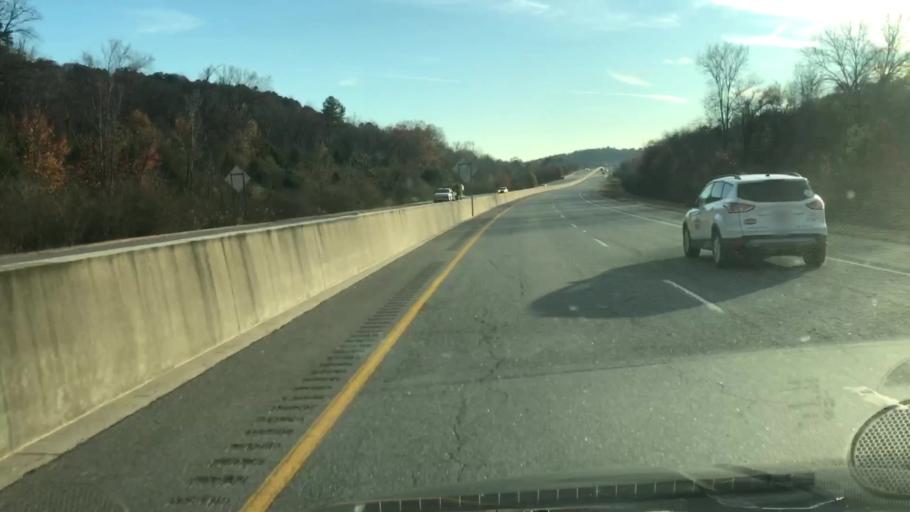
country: US
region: Arkansas
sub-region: Garland County
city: Hot Springs
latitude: 34.4823
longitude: -92.9825
